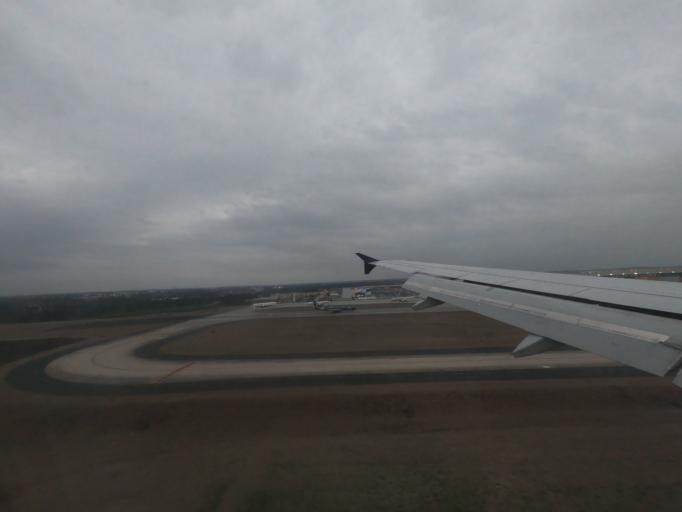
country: US
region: Georgia
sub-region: Fulton County
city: Hapeville
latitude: 33.6494
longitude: -84.4072
